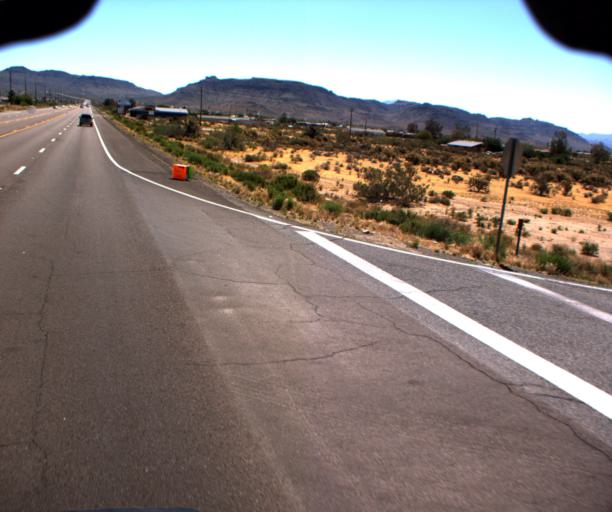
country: US
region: Arizona
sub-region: Mohave County
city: Golden Valley
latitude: 35.2203
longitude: -114.1831
